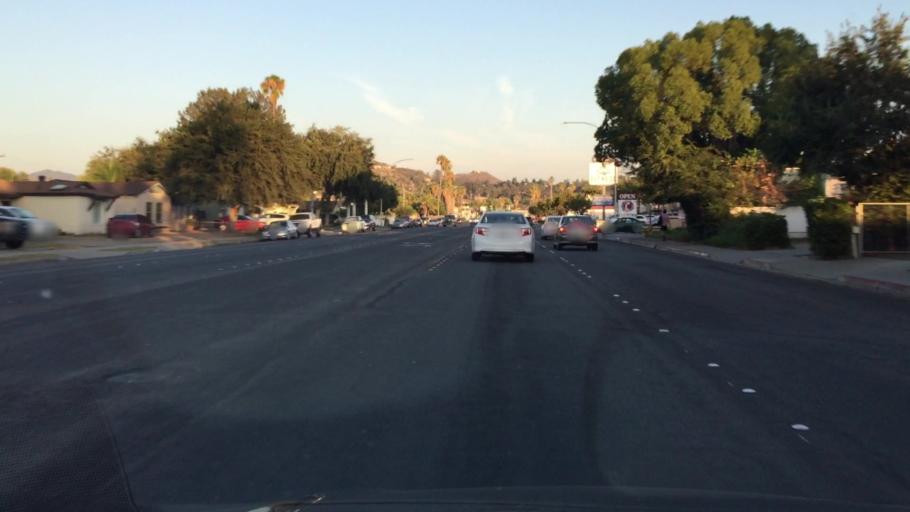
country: US
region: California
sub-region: San Diego County
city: Bostonia
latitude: 32.7907
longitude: -116.9316
